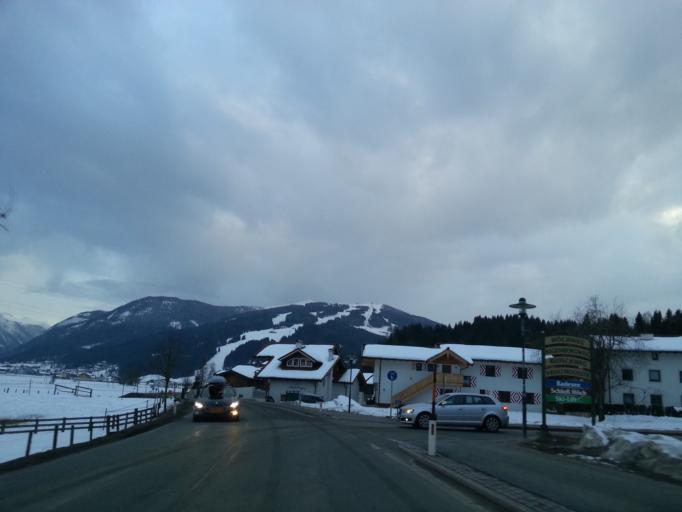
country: AT
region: Salzburg
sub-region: Politischer Bezirk Sankt Johann im Pongau
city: Flachau
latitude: 47.3716
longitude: 13.3876
